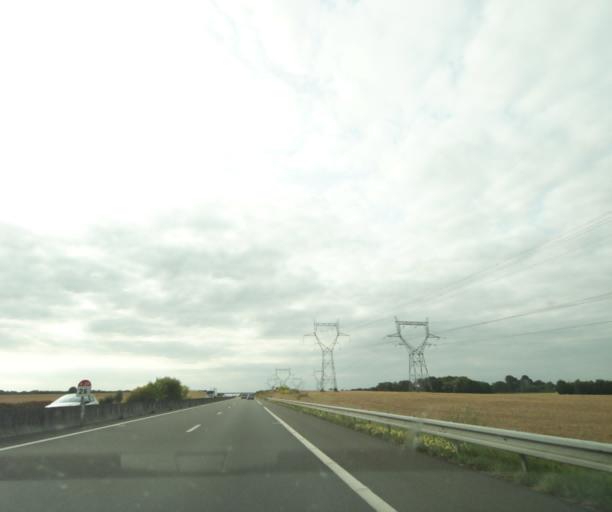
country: FR
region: Centre
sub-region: Departement d'Indre-et-Loire
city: Cerelles
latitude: 47.4916
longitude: 0.6641
